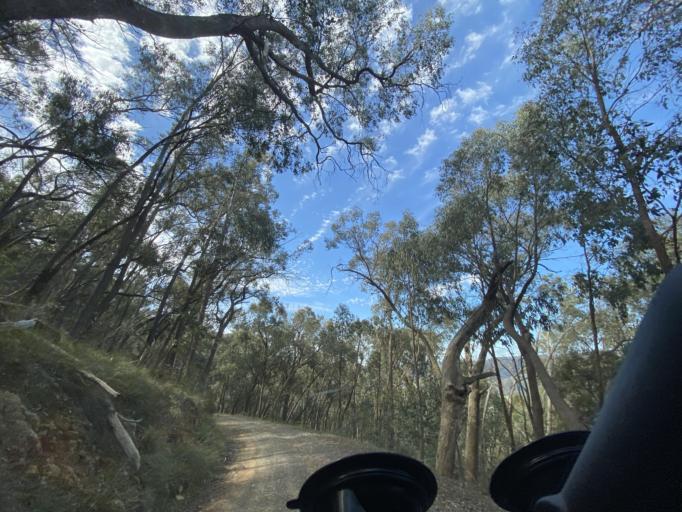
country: AU
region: Victoria
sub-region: Mansfield
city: Mansfield
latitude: -36.7997
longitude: 146.1123
